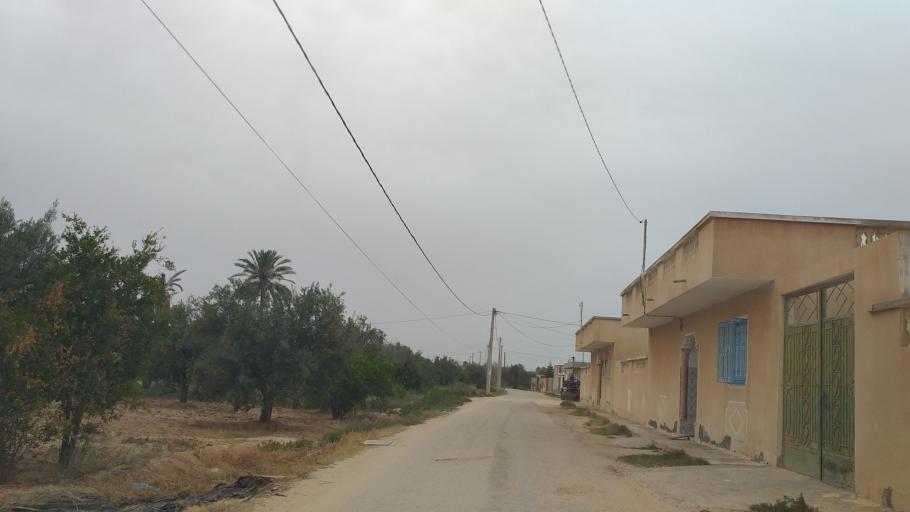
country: TN
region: Qabis
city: Gabes
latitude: 33.9508
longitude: 10.0607
